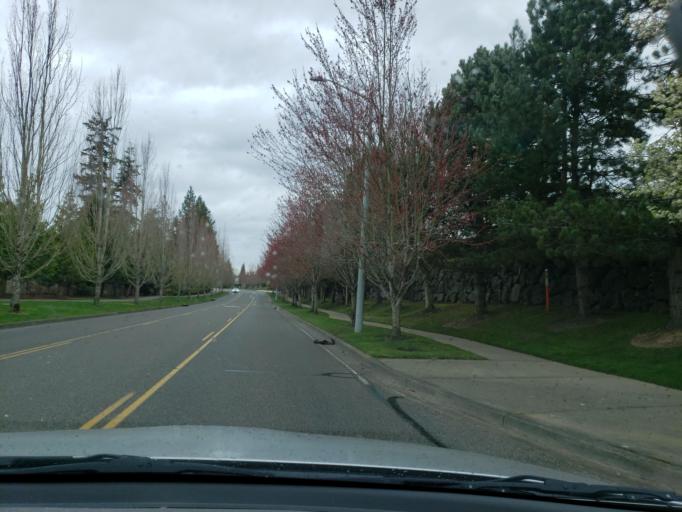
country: US
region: Washington
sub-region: Snohomish County
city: Meadowdale
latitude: 47.8900
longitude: -122.2954
